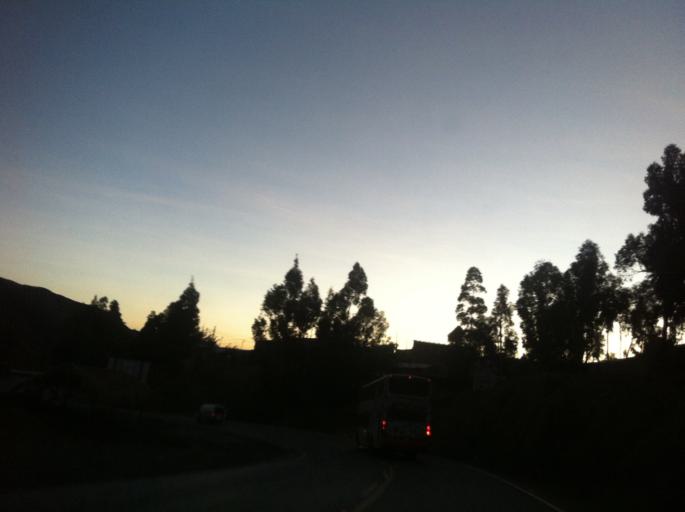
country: BO
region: Cochabamba
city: Irpa Irpa
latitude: -17.6662
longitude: -66.4124
